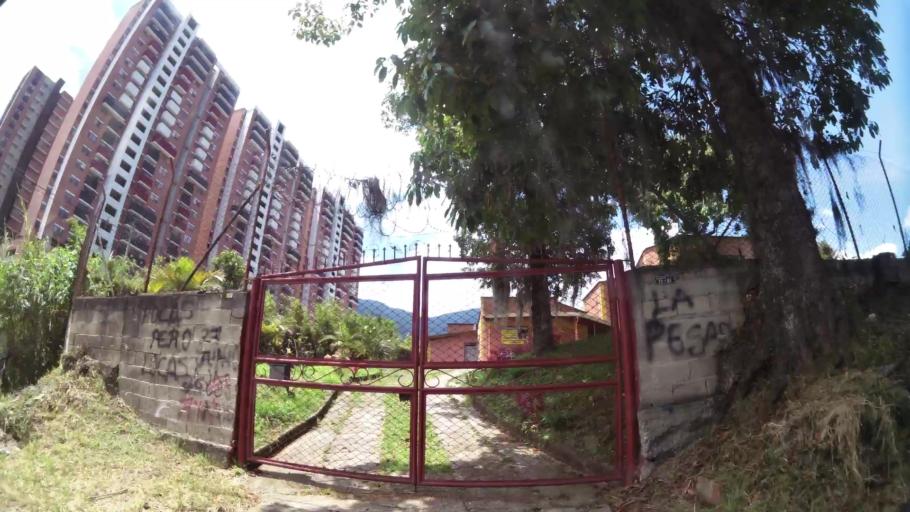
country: CO
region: Antioquia
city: La Estrella
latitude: 6.1656
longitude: -75.6454
